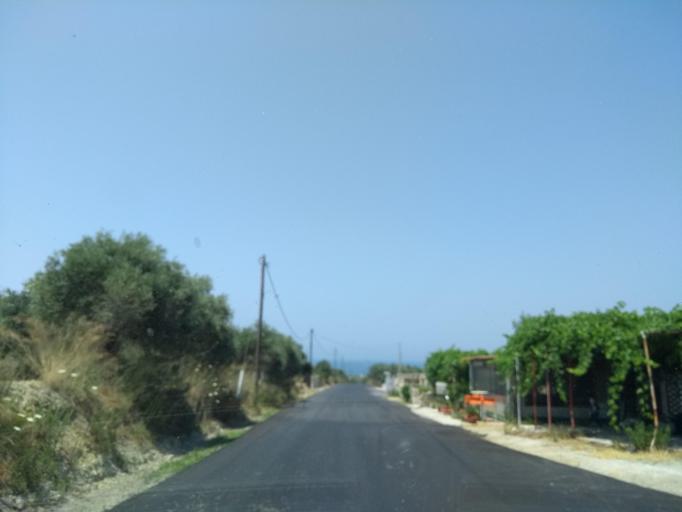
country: GR
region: Crete
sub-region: Nomos Chanias
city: Georgioupolis
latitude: 35.3330
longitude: 24.3016
